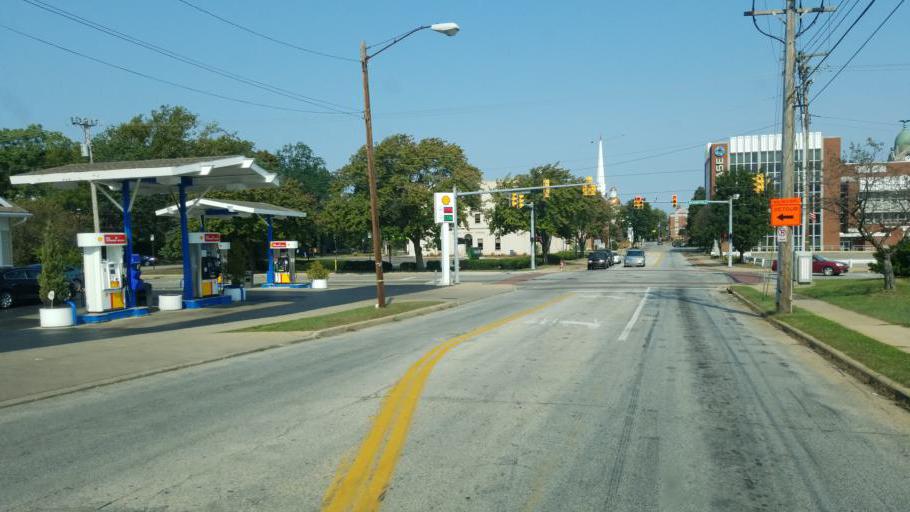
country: US
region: Ohio
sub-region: Lake County
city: Painesville
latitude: 41.7222
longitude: -81.2435
